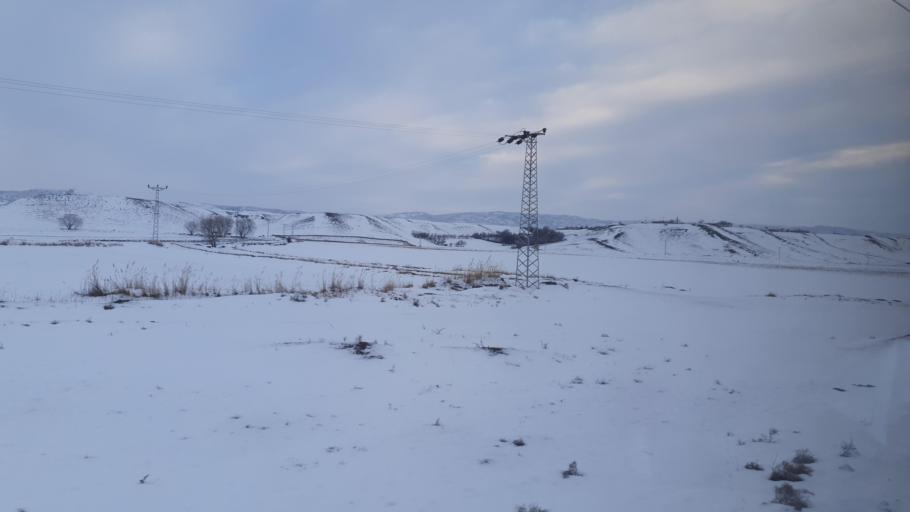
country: TR
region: Kirsehir
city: Mecidiye
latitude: 39.6861
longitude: 34.3987
